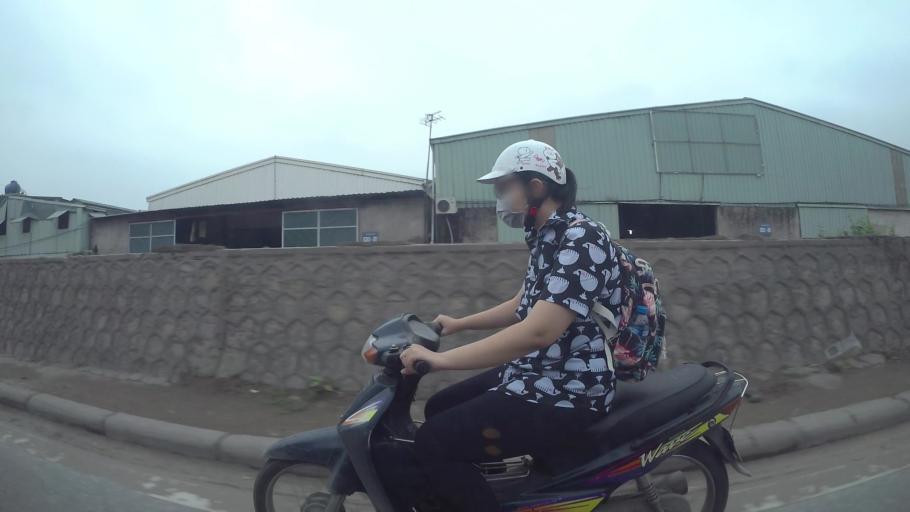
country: VN
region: Ha Noi
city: Hai BaTrung
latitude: 21.0013
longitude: 105.8783
